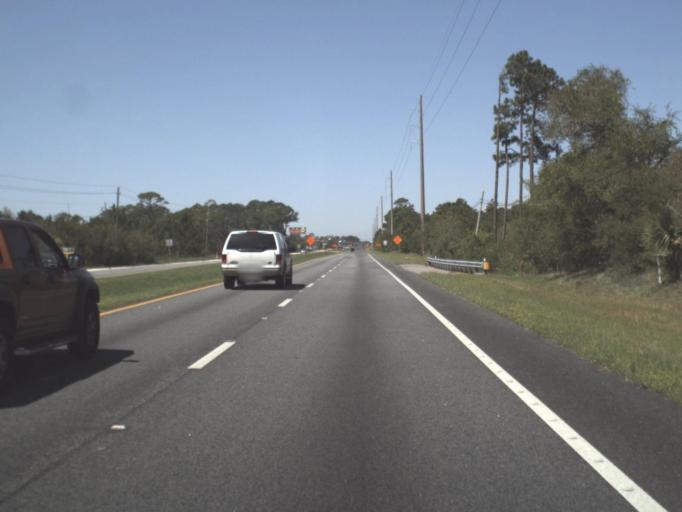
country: US
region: Florida
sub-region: Santa Rosa County
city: Navarre
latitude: 30.4101
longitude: -86.7921
